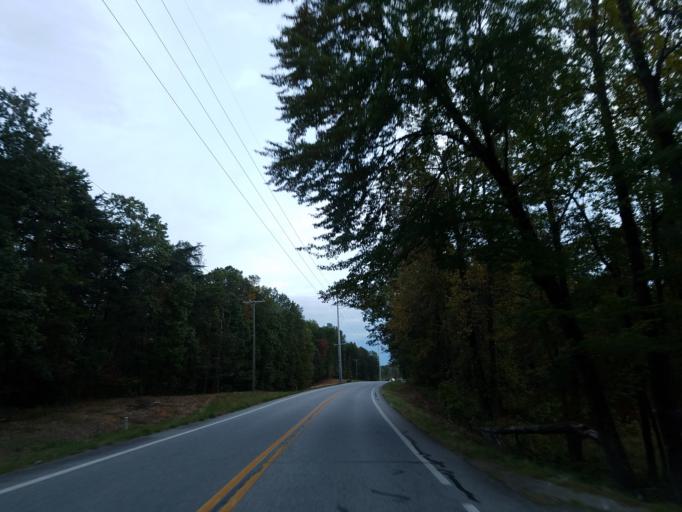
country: US
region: Georgia
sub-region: Dawson County
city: Dawsonville
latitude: 34.4629
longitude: -84.1748
